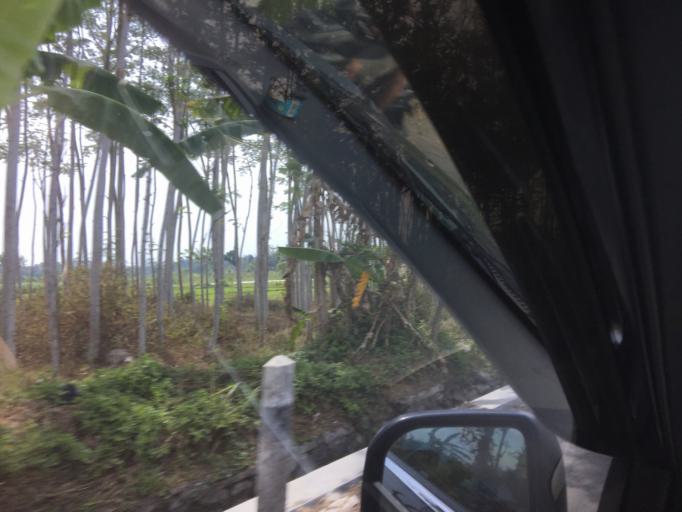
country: ID
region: Central Java
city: Candi Prambanan
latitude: -7.7515
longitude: 110.4810
